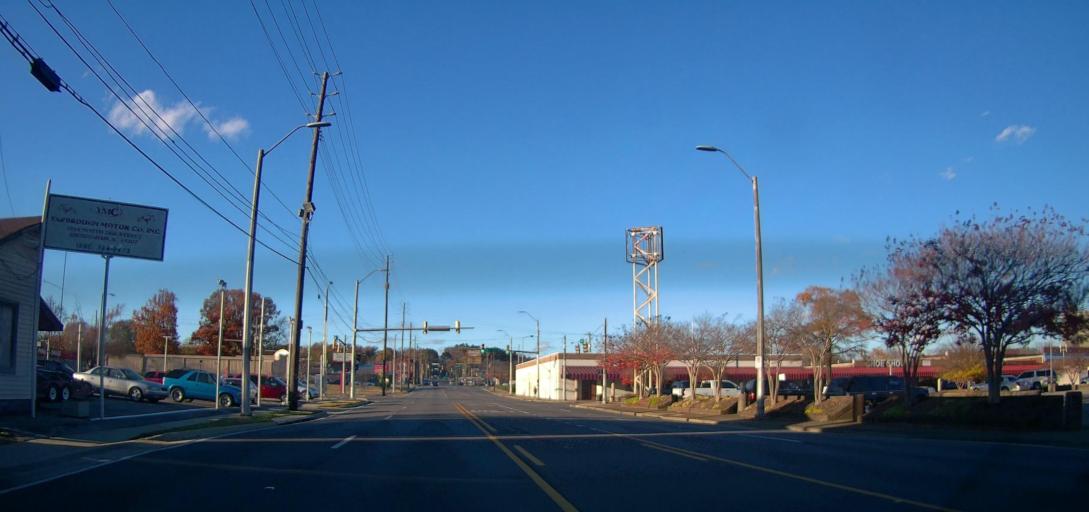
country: US
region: Alabama
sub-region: Jefferson County
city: Birmingham
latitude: 33.5522
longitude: -86.8182
